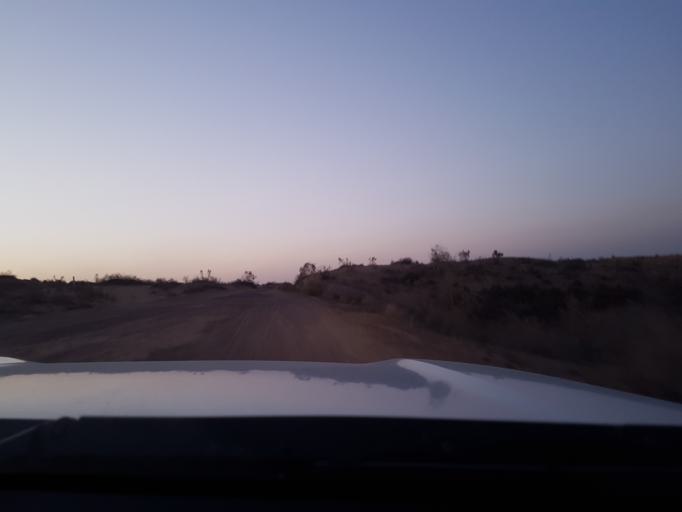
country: UZ
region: Xorazm
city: Khiwa
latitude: 41.3233
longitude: 60.2039
